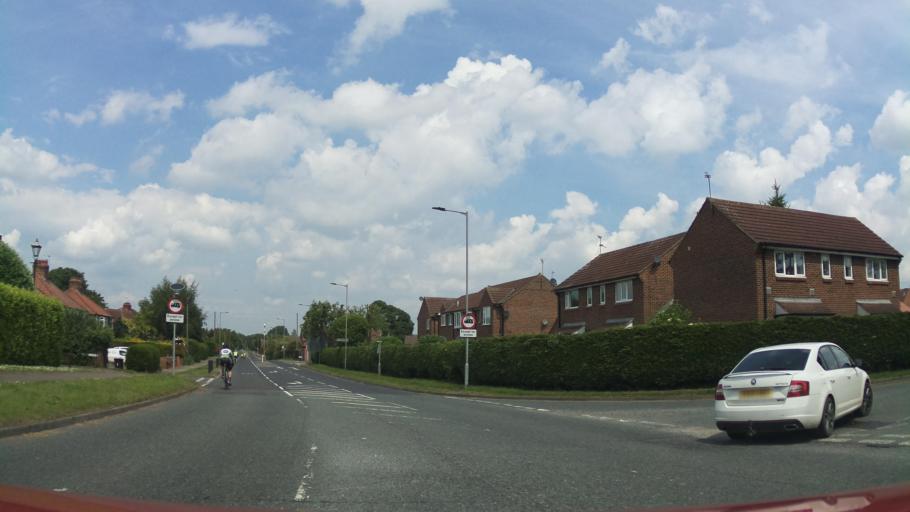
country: GB
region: England
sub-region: North Yorkshire
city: Boroughbridge
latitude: 54.0832
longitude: -1.3954
